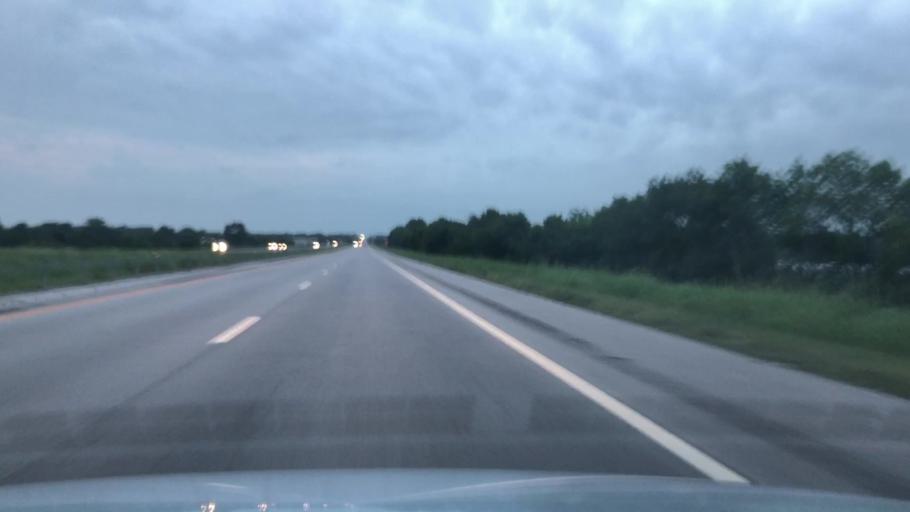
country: US
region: Oklahoma
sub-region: Washington County
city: Bartlesville
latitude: 36.6579
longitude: -95.9352
